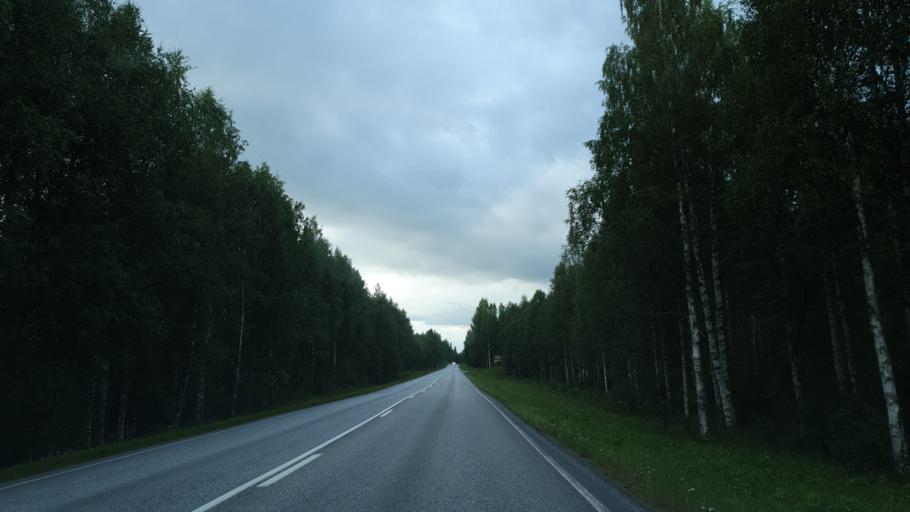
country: FI
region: North Karelia
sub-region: Joensuu
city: Eno
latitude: 63.0496
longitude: 30.1264
